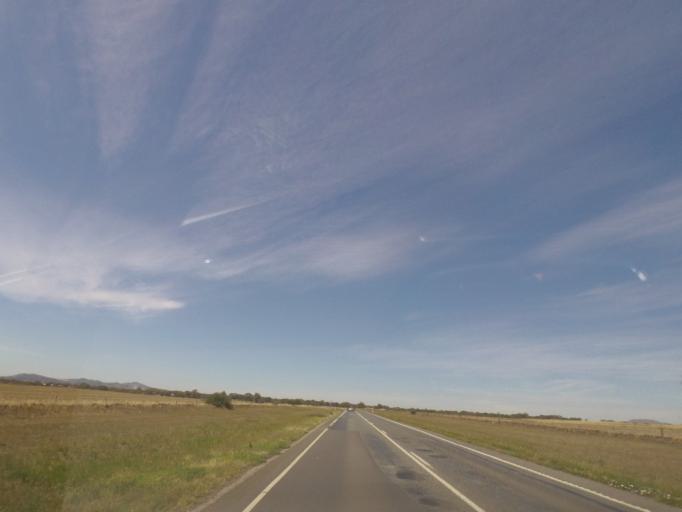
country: AU
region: Victoria
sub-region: Wyndham
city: Wyndham Vale
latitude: -37.8451
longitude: 144.3878
